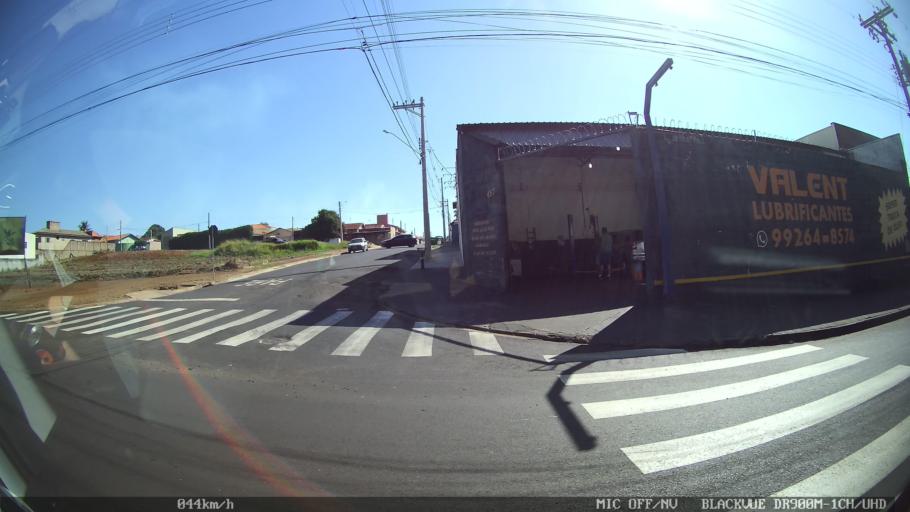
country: BR
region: Sao Paulo
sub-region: Batatais
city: Batatais
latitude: -20.8828
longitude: -47.5950
